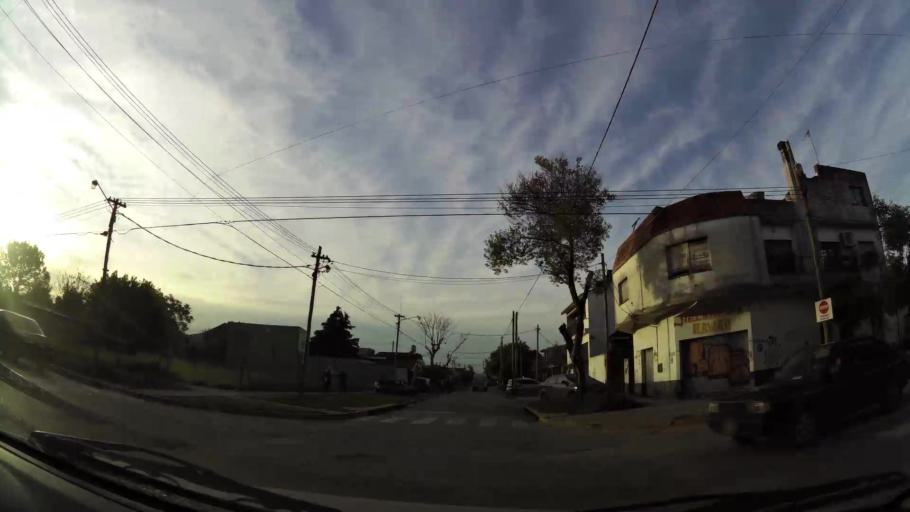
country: AR
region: Buenos Aires
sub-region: Partido de Almirante Brown
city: Adrogue
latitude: -34.7916
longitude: -58.3524
